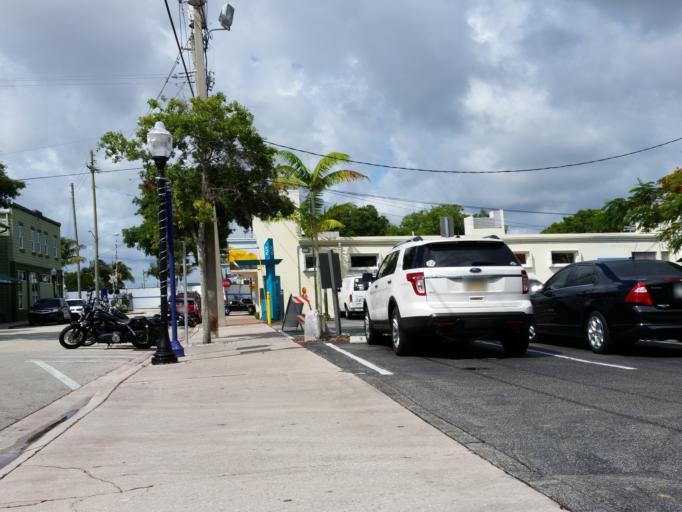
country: US
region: Florida
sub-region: Martin County
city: Stuart
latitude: 27.2002
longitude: -80.2544
